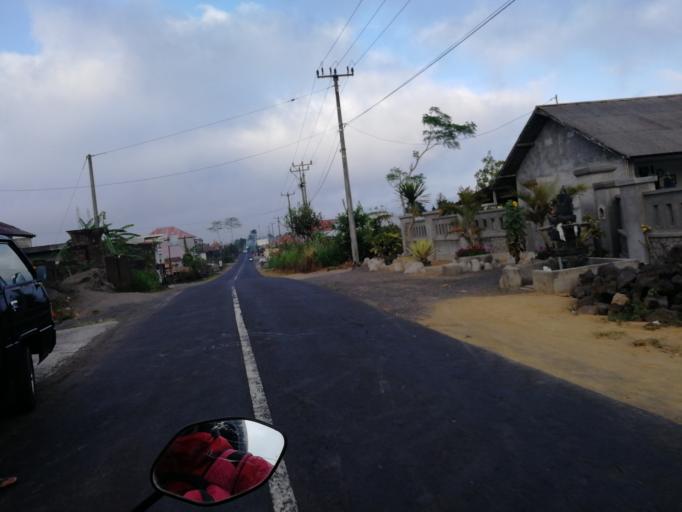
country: ID
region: Bali
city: Banjar Kedisan
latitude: -8.2227
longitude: 115.2626
